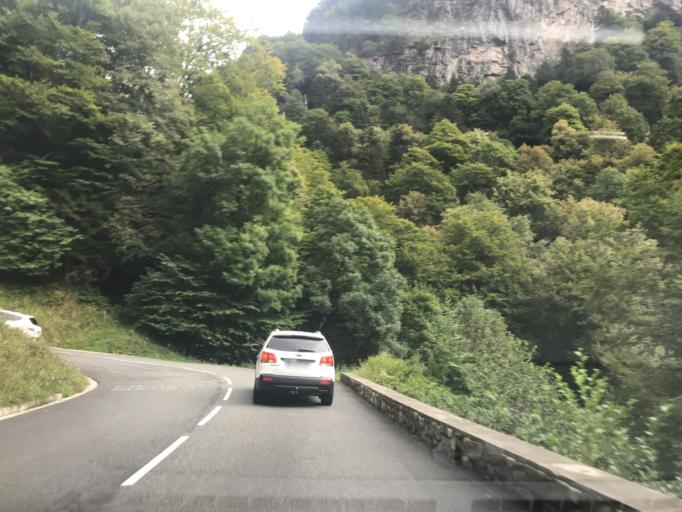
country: FR
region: Midi-Pyrenees
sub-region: Departement de la Haute-Garonne
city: Bagneres-de-Luchon
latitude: 42.7703
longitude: 0.6518
